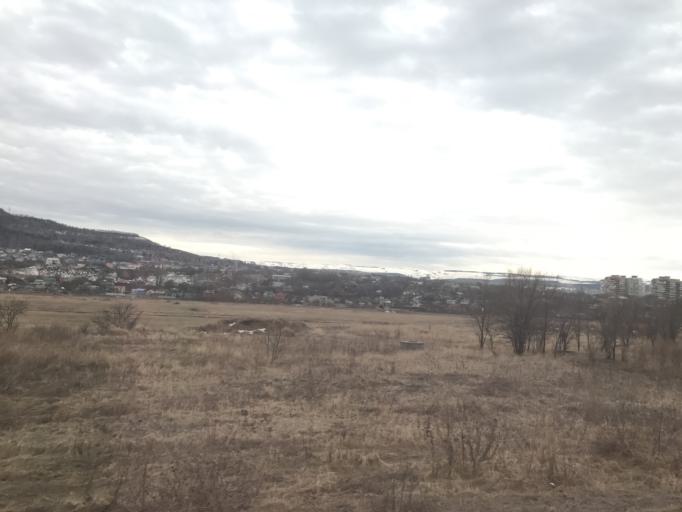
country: RU
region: Stavropol'skiy
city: Kislovodsk
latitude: 43.9473
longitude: 42.7372
